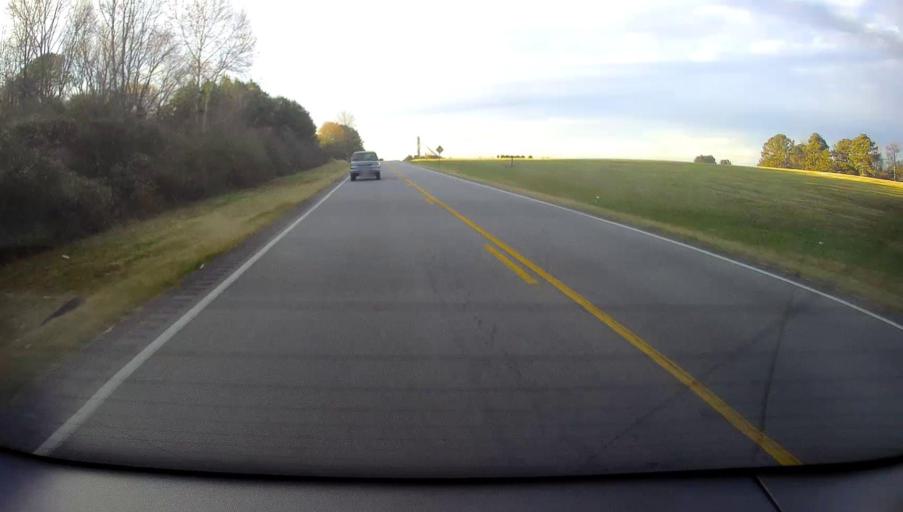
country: US
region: Alabama
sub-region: Blount County
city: Oneonta
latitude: 34.1019
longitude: -86.3677
